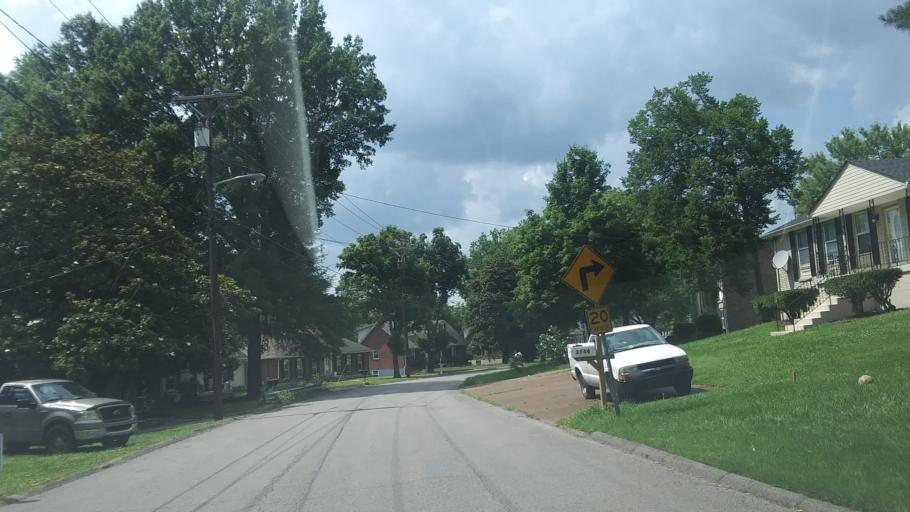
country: US
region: Tennessee
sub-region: Davidson County
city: Oak Hill
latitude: 36.0740
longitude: -86.7110
